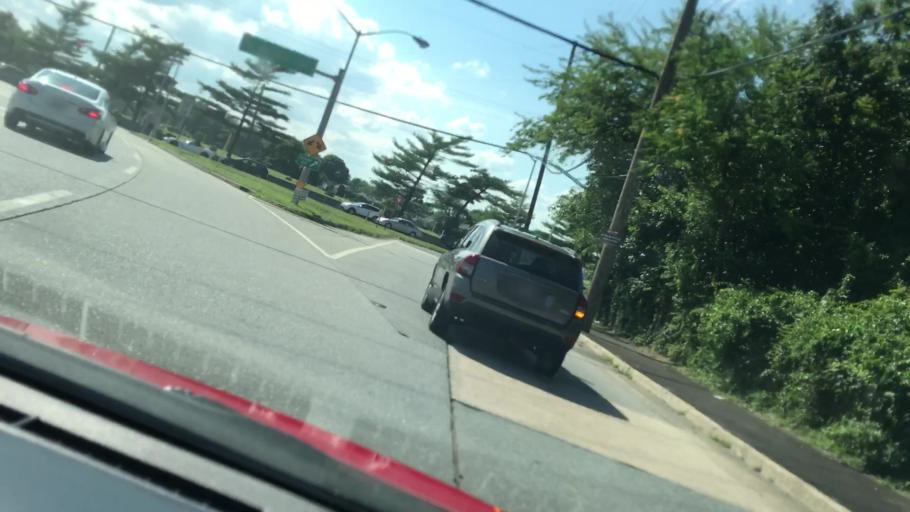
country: US
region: New York
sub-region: Nassau County
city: Rockville Centre
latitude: 40.6592
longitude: -73.6563
